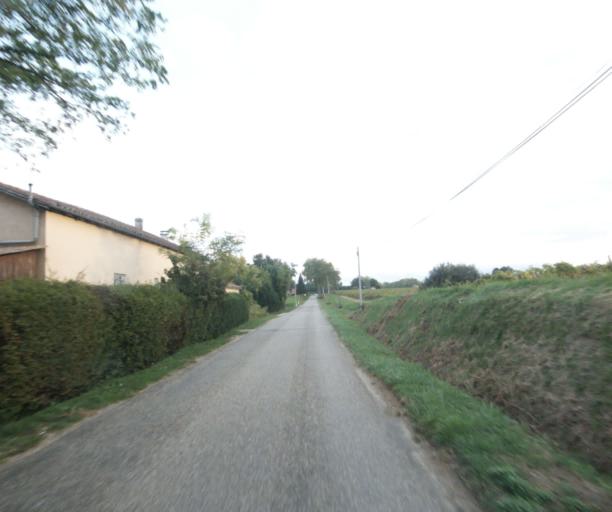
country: FR
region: Aquitaine
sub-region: Departement des Landes
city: Gabarret
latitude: 43.9731
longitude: 0.0937
